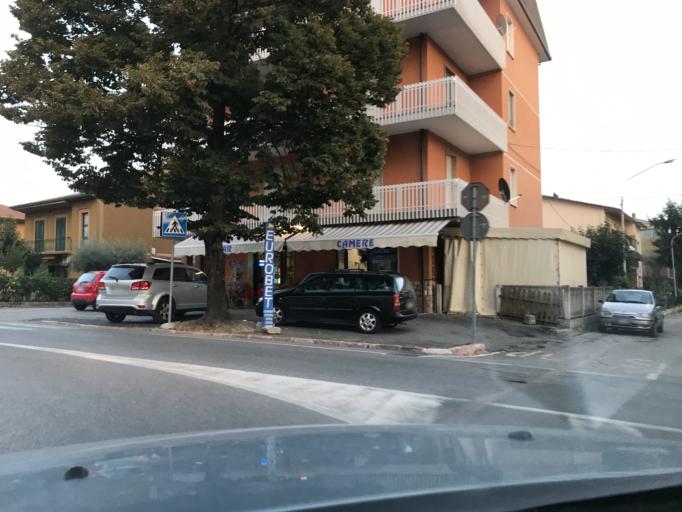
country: IT
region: Umbria
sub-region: Provincia di Perugia
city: Ponte Felcino
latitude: 43.0869
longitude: 12.4301
